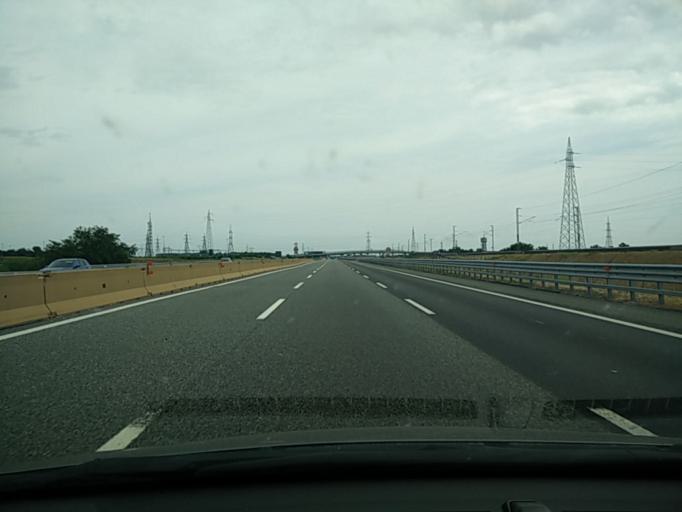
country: IT
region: Piedmont
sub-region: Provincia di Torino
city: Chivasso
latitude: 45.2253
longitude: 7.9278
